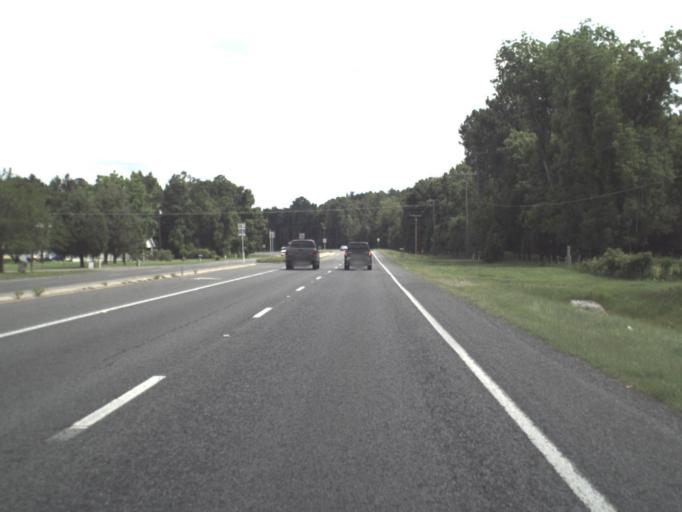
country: US
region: Florida
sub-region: Nassau County
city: Nassau Village-Ratliff
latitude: 30.5118
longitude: -81.7935
